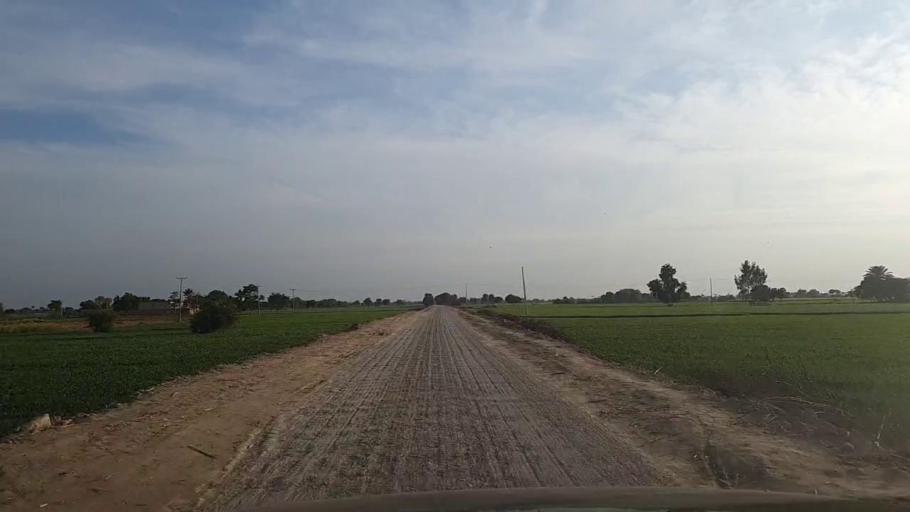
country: PK
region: Sindh
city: Jam Sahib
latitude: 26.4446
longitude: 68.5717
